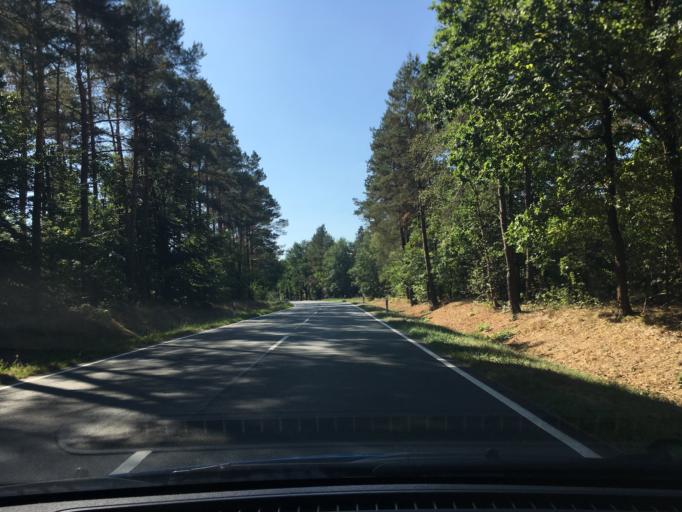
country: DE
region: Lower Saxony
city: Wietzendorf
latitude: 52.8750
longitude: 9.9820
